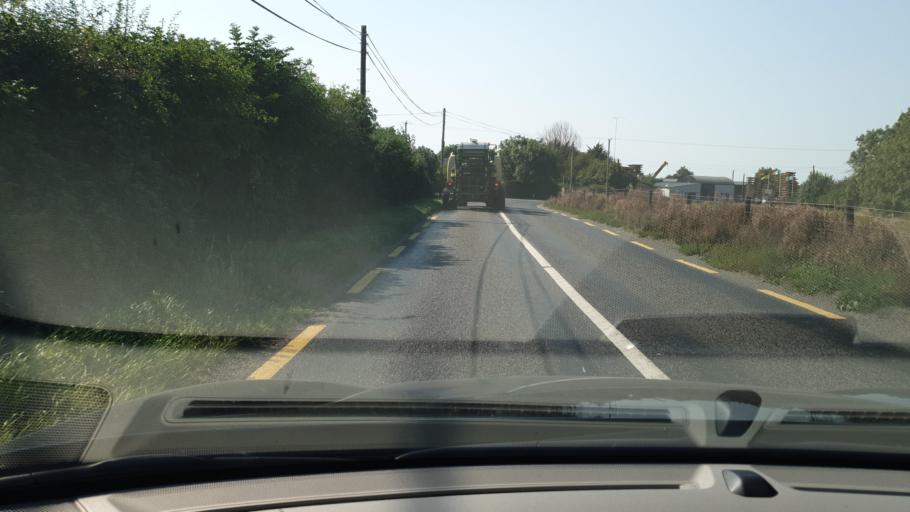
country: IE
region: Leinster
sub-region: An Mhi
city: Trim
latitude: 53.5831
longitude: -6.8529
